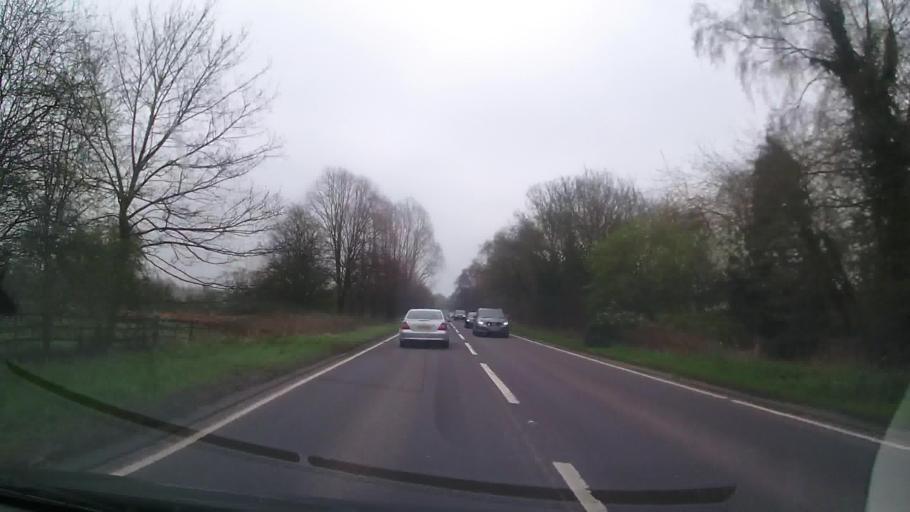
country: GB
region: England
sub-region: Shropshire
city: Market Drayton
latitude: 52.9124
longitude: -2.4867
